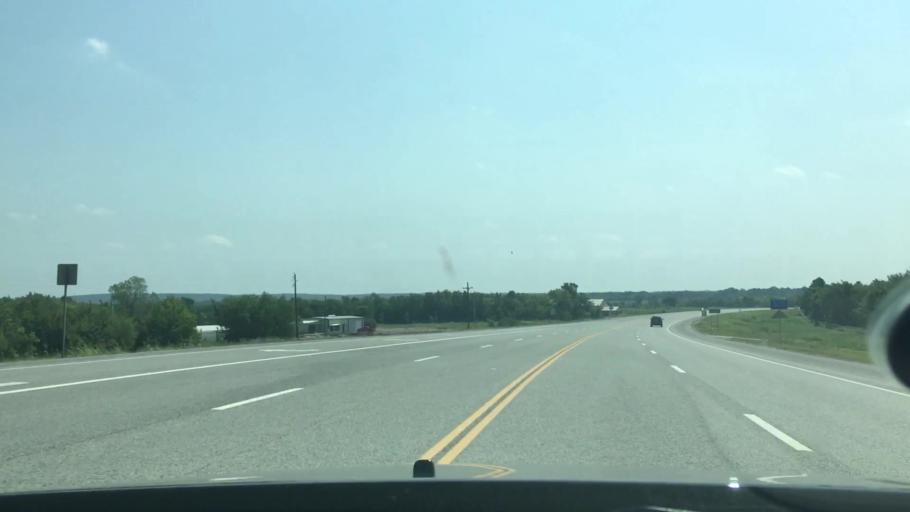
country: US
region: Oklahoma
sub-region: Atoka County
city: Atoka
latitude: 34.3728
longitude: -96.1100
